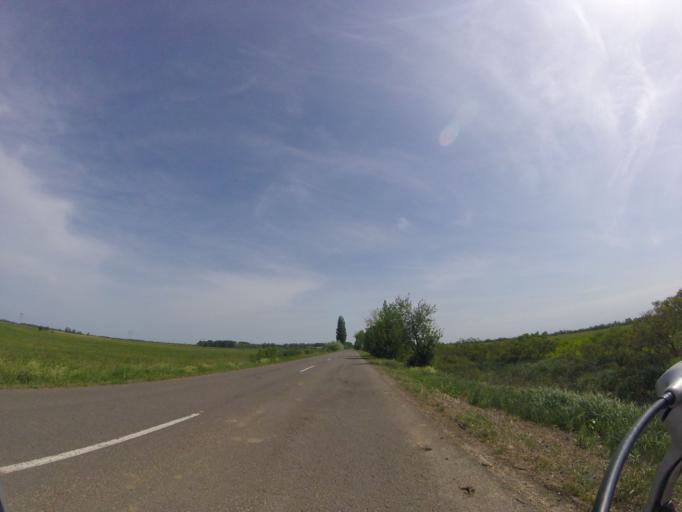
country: HU
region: Jasz-Nagykun-Szolnok
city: Tiszapuspoki
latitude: 47.2742
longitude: 20.3598
